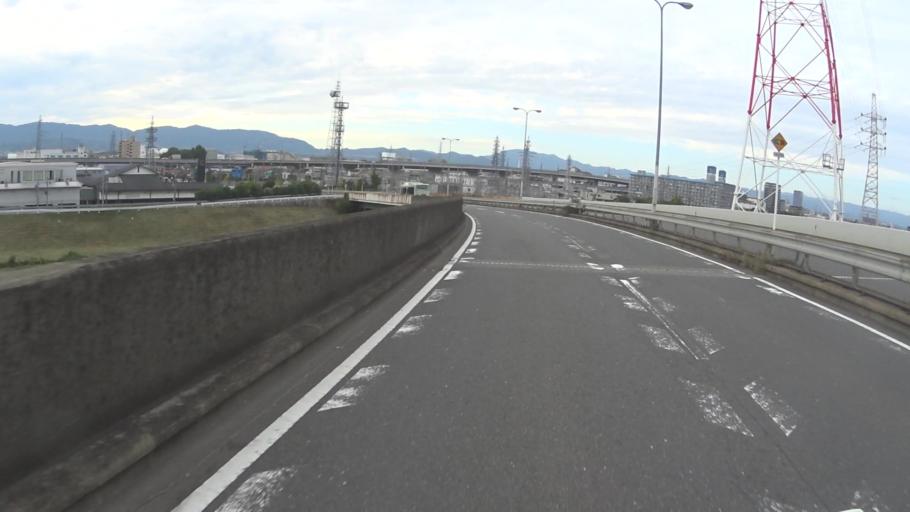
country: JP
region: Kyoto
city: Uji
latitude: 34.9252
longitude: 135.7545
